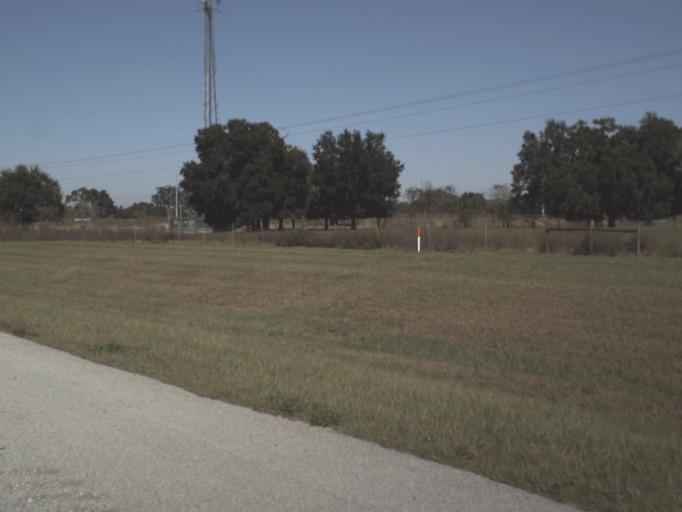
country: US
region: Florida
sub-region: Sumter County
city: Wildwood
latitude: 28.7947
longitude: -81.9937
